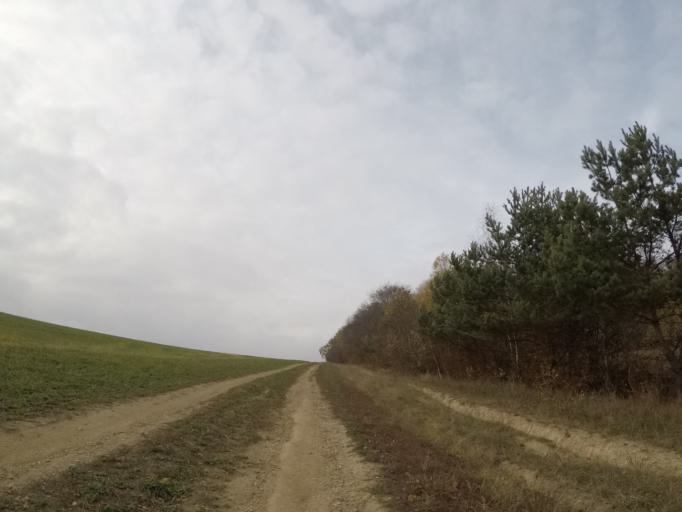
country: SK
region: Presovsky
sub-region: Okres Presov
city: Presov
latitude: 48.9298
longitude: 21.1355
